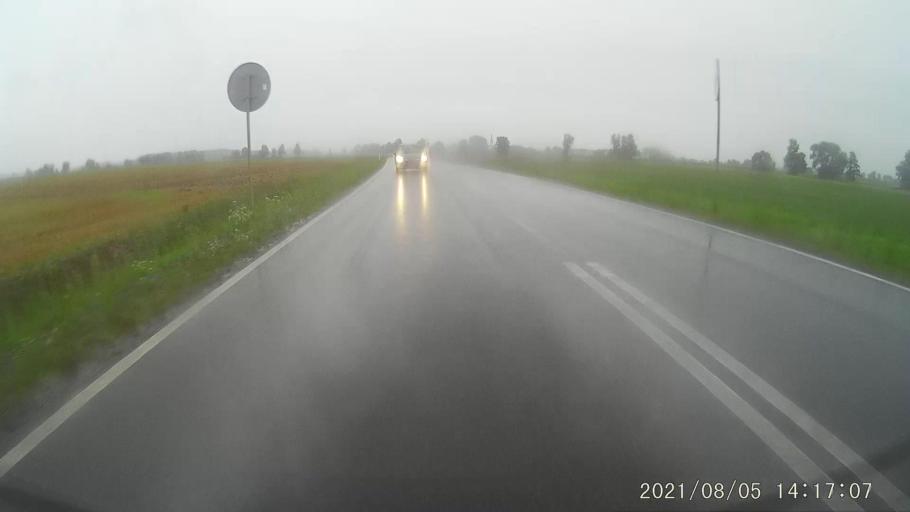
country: PL
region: Opole Voivodeship
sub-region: Powiat prudnicki
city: Biala
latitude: 50.4595
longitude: 17.7115
